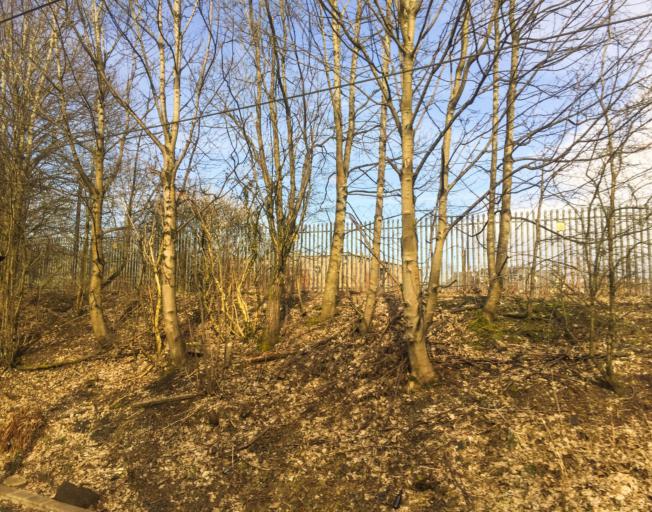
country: GB
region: Scotland
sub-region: North Lanarkshire
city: Coatbridge
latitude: 55.8511
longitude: -4.0140
